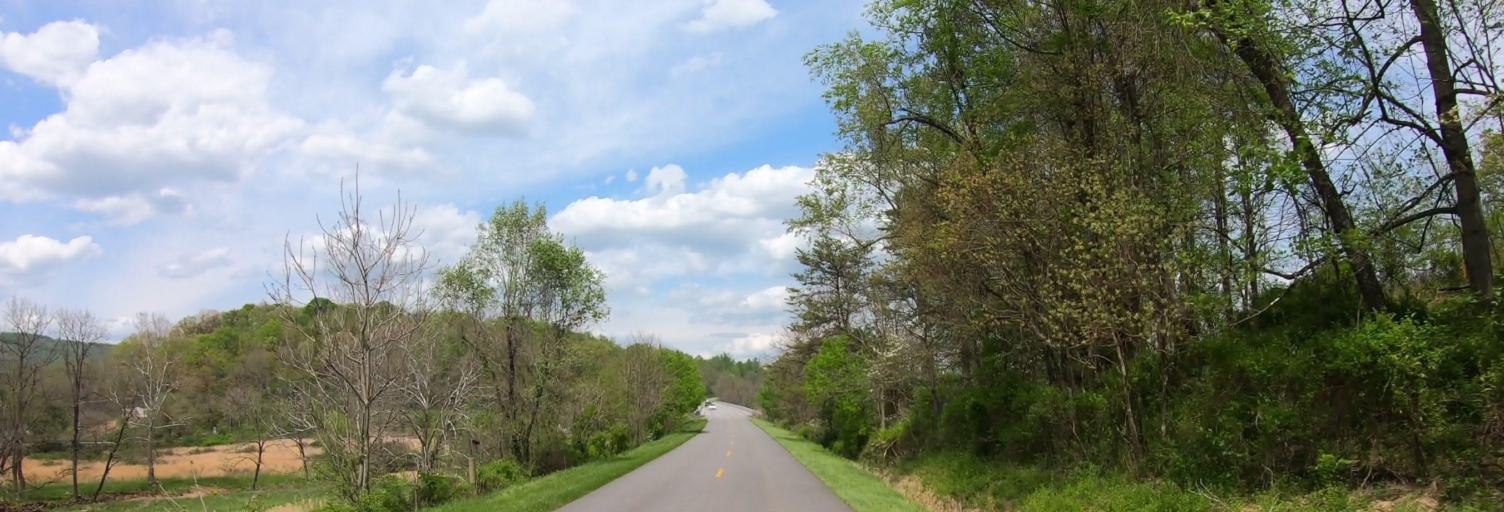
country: US
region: Virginia
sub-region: Botetourt County
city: Laymantown
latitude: 37.3338
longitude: -79.8529
